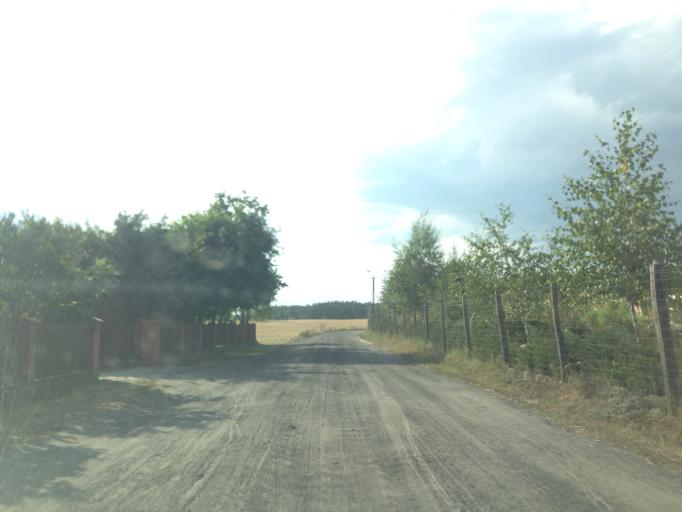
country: PL
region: Kujawsko-Pomorskie
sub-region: Powiat swiecki
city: Swiekatowo
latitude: 53.4917
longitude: 18.1310
